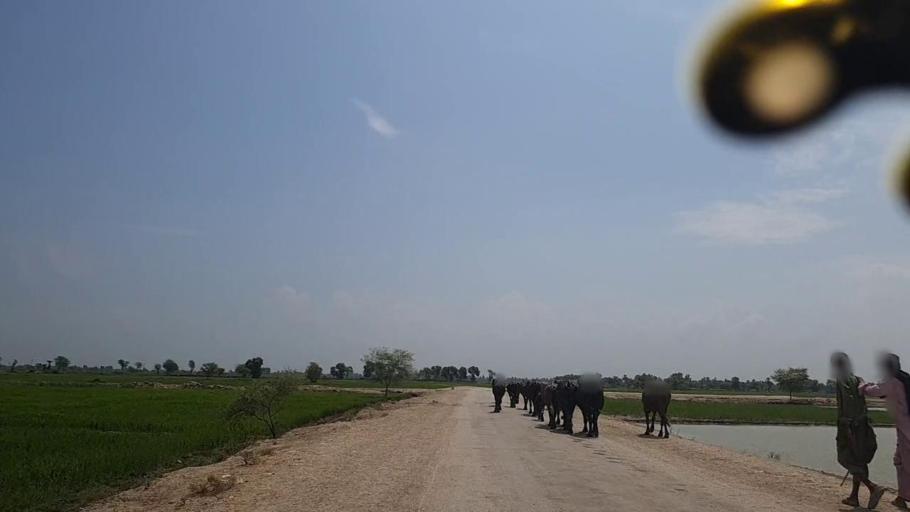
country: PK
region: Sindh
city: Thul
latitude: 28.1151
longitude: 68.8589
